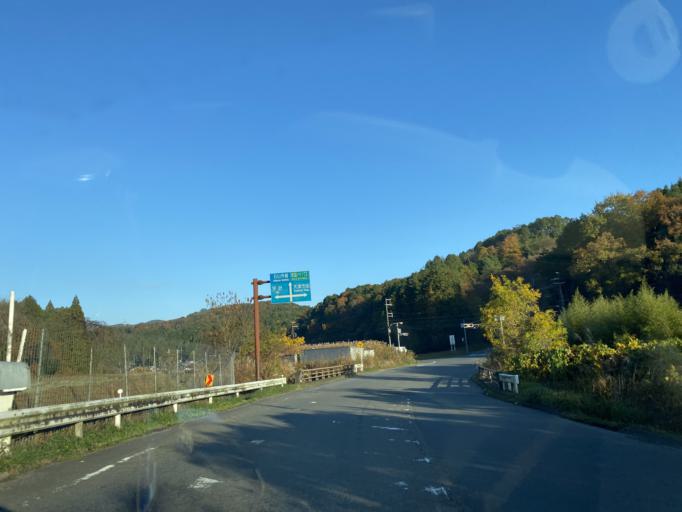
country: JP
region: Kyoto
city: Uji
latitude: 34.9005
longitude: 135.8828
